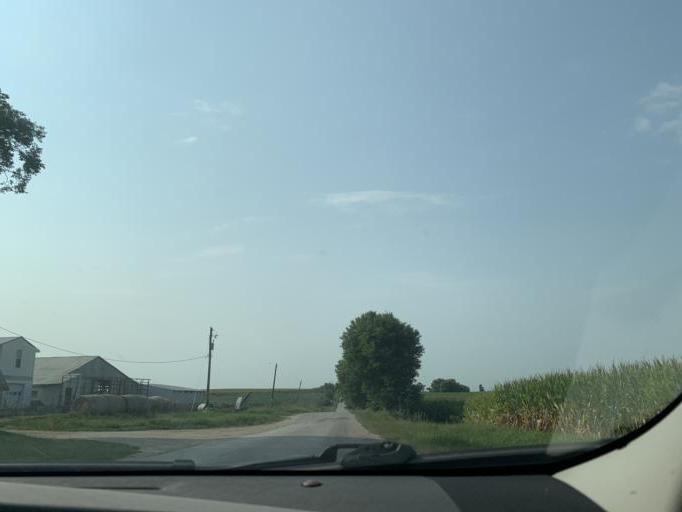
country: US
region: Illinois
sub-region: Whiteside County
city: Sterling
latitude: 41.8336
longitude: -89.7471
